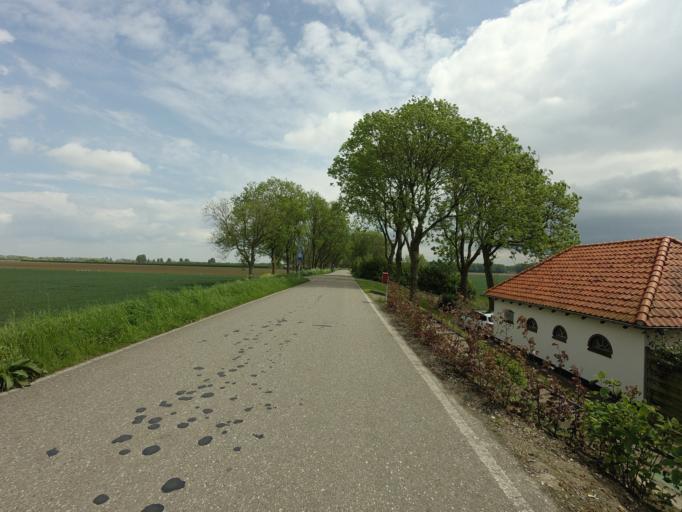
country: NL
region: North Brabant
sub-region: Gemeente Moerdijk
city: Willemstad
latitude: 51.7295
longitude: 4.4643
